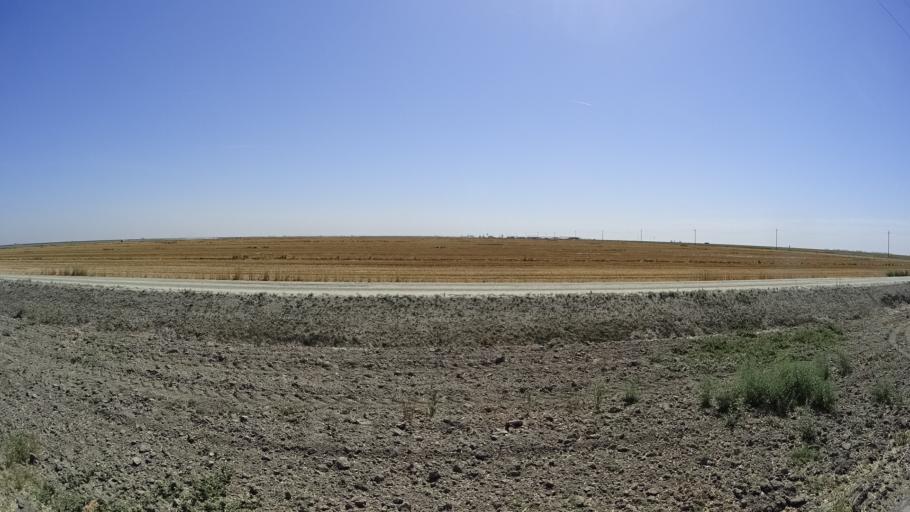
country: US
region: California
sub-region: Kings County
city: Corcoran
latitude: 35.9944
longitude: -119.5362
